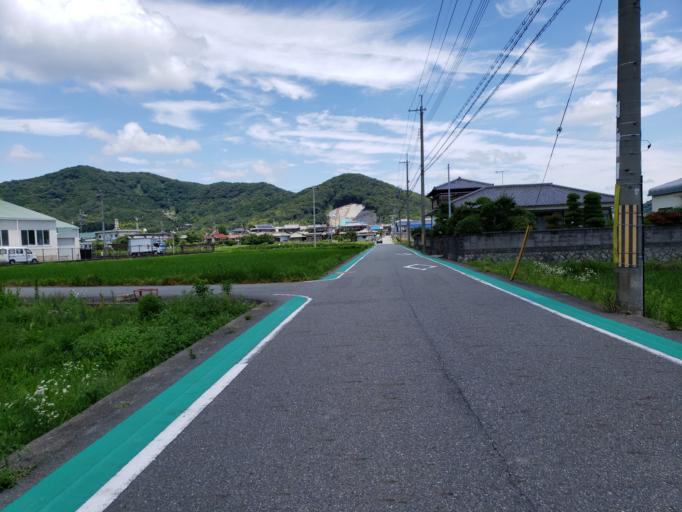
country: JP
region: Hyogo
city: Kakogawacho-honmachi
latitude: 34.8193
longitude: 134.8106
